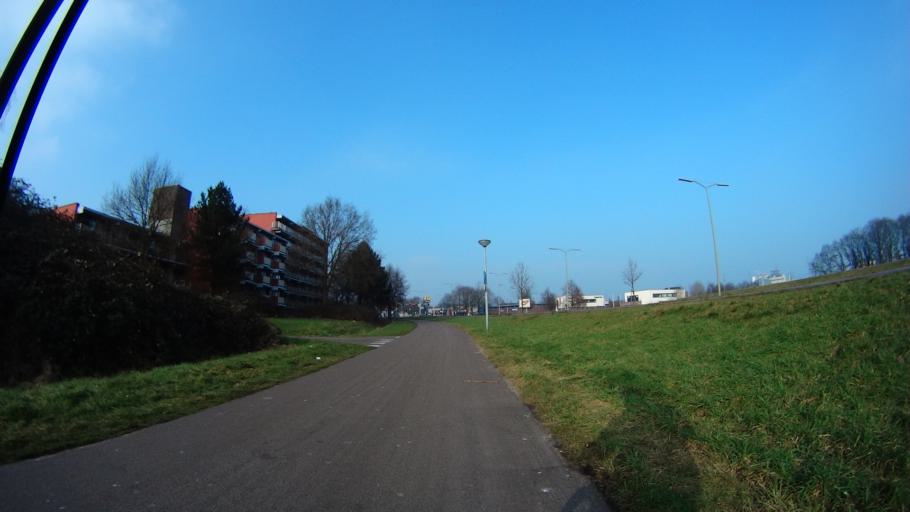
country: NL
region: Drenthe
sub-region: Gemeente Emmen
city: Emmen
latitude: 52.7695
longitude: 6.8967
